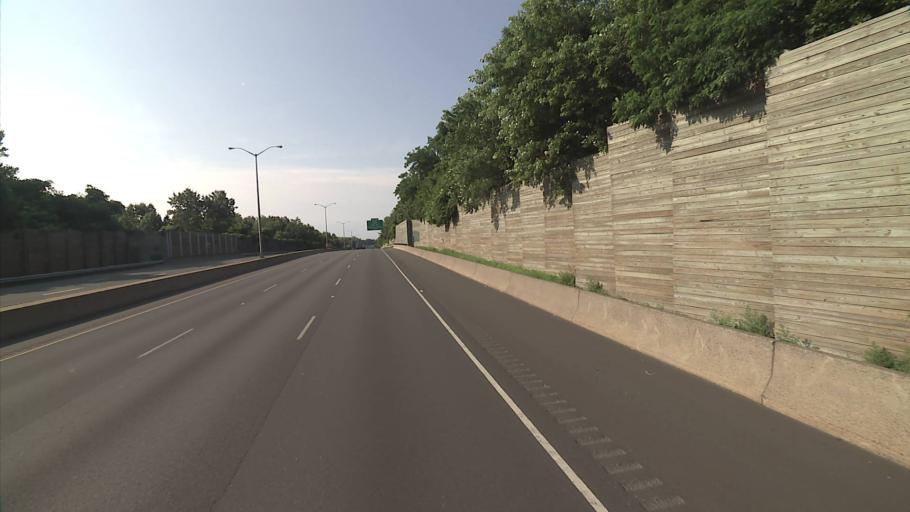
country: US
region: Connecticut
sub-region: Hartford County
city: Thompsonville
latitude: 42.0148
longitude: -72.5868
